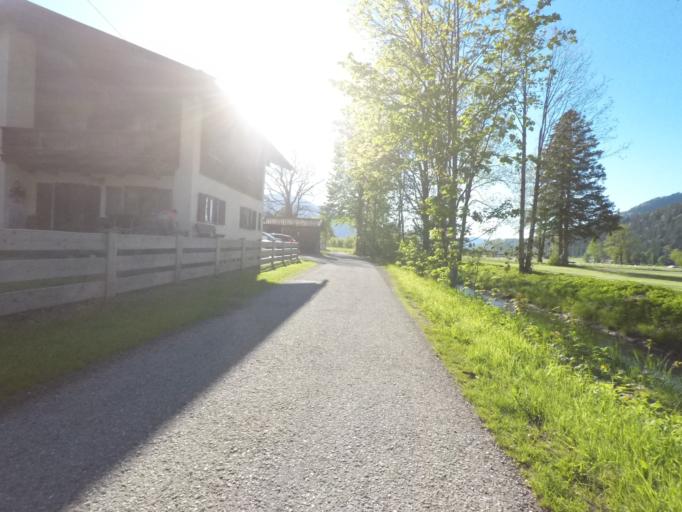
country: DE
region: Bavaria
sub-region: Upper Bavaria
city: Bayrischzell
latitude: 47.6737
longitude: 12.0066
